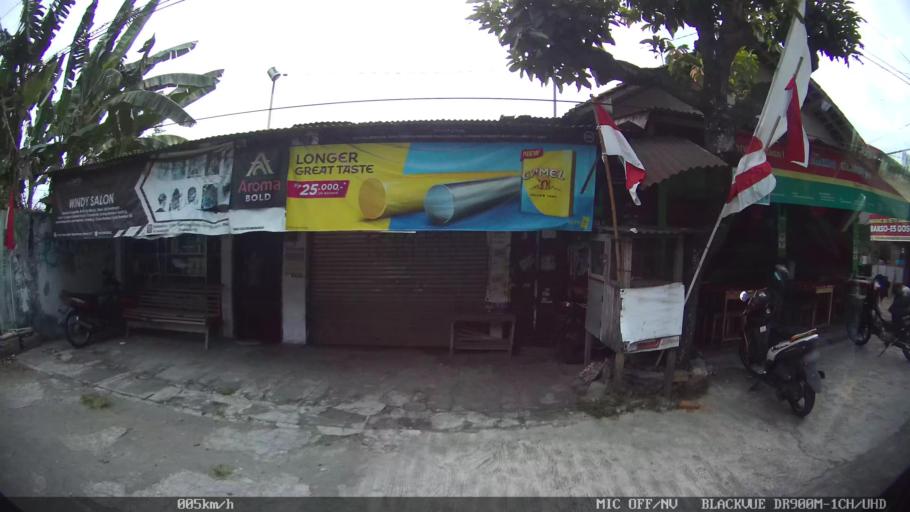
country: ID
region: Daerah Istimewa Yogyakarta
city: Yogyakarta
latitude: -7.7927
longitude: 110.3982
